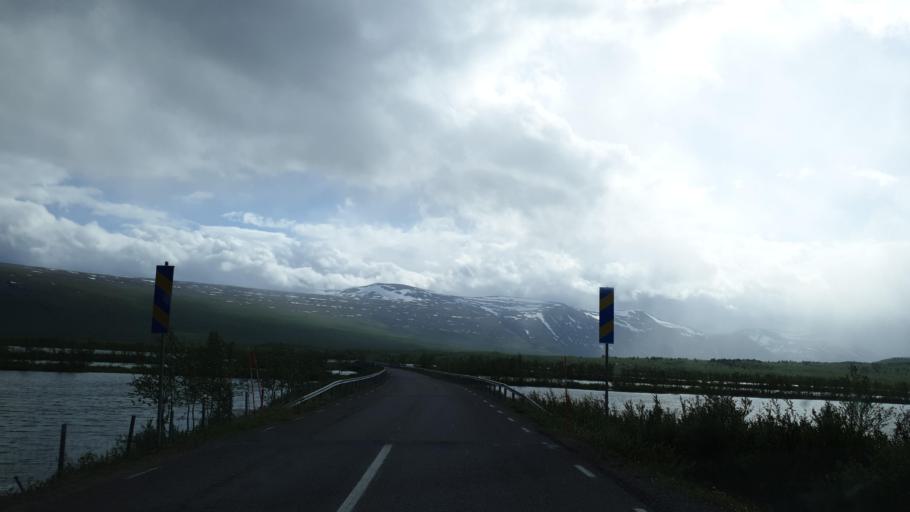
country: SE
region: Norrbotten
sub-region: Kiruna Kommun
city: Kiruna
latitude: 67.8618
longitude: 19.0318
